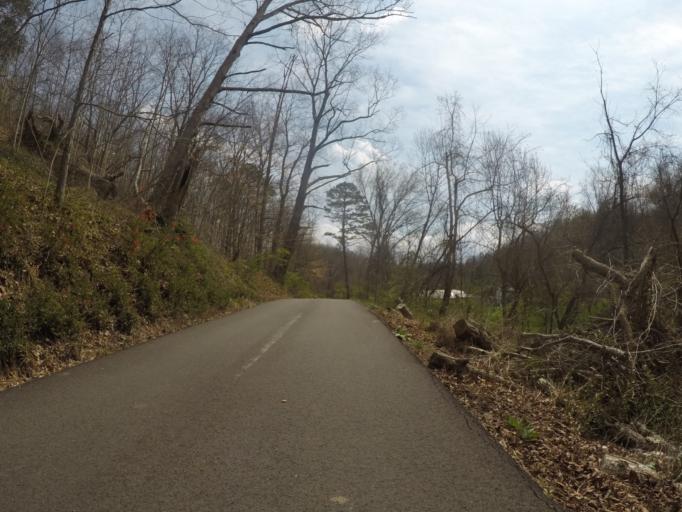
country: US
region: West Virginia
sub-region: Cabell County
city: Pea Ridge
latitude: 38.3939
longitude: -82.3500
